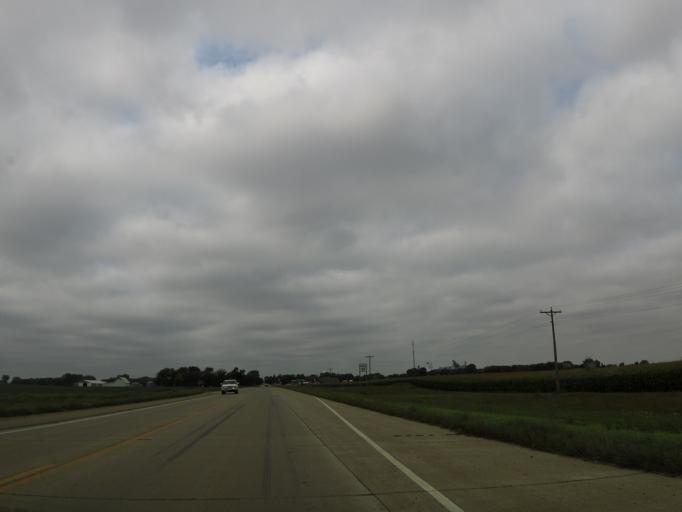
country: US
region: Minnesota
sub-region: Renville County
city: Renville
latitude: 44.7894
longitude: -95.1928
